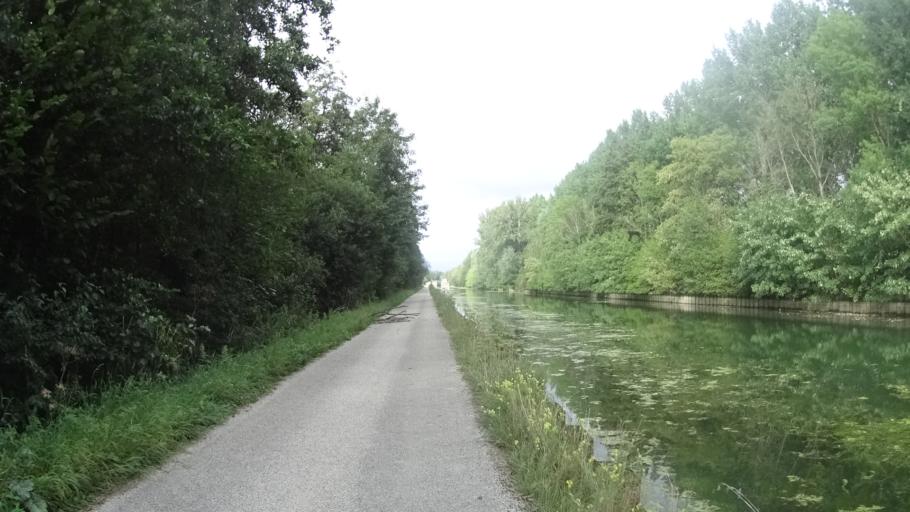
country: FR
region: Picardie
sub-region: Departement de l'Aisne
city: Itancourt
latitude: 49.7640
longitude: 3.3856
